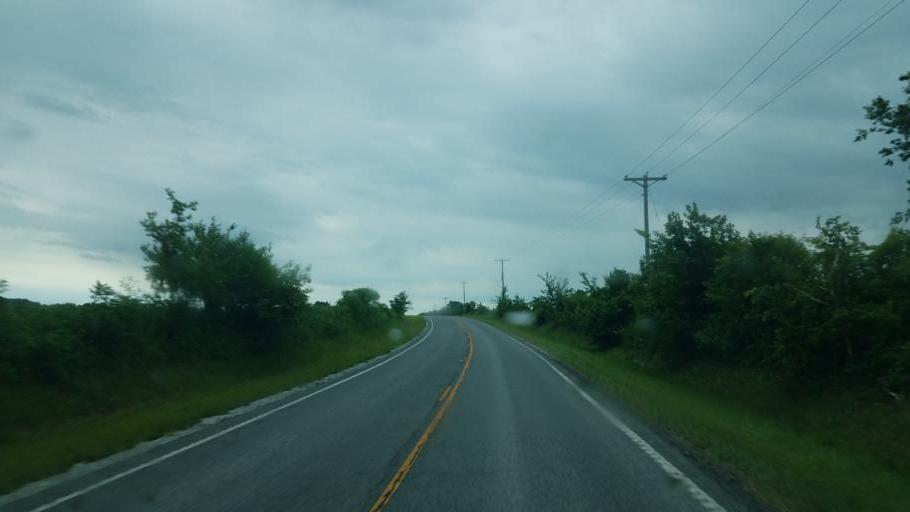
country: US
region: Missouri
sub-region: Cooper County
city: Boonville
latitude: 38.8370
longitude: -92.6215
